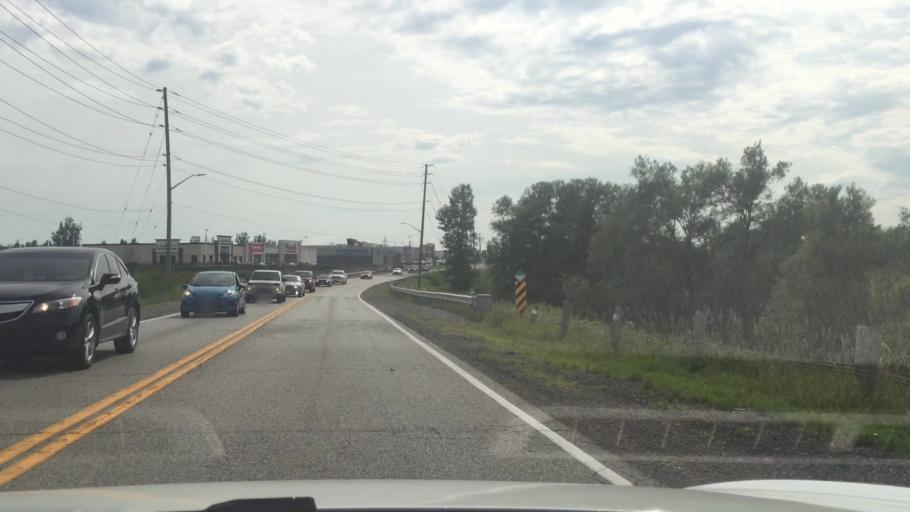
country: CA
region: Ontario
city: Oshawa
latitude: 43.8703
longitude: -78.8942
